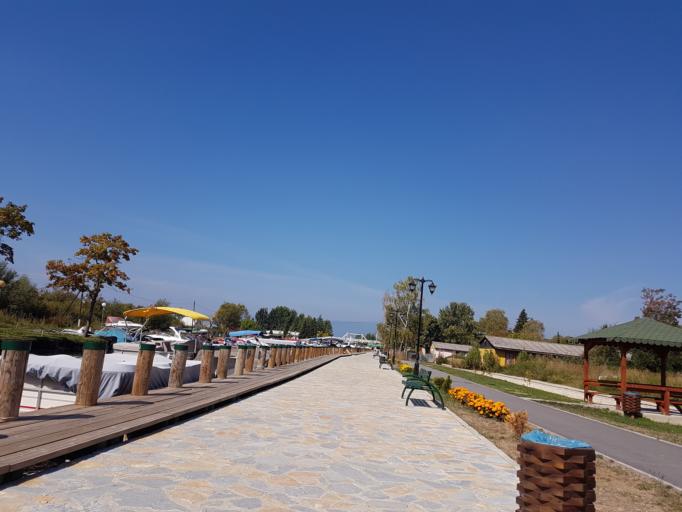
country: MK
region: Ohrid
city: Ohrid
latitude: 41.1034
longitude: 20.8105
